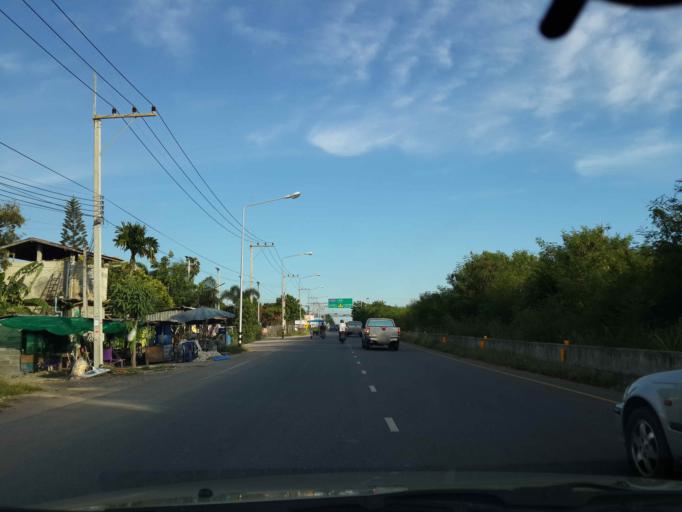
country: TH
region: Chon Buri
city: Phatthaya
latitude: 12.8847
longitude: 100.9036
